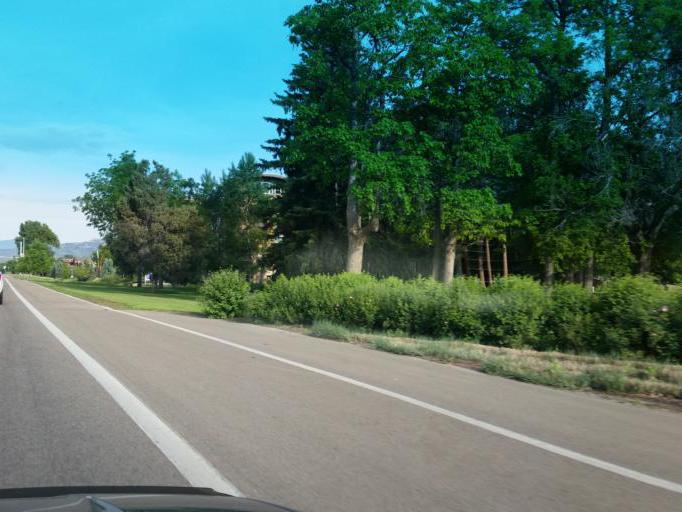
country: US
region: Colorado
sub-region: Larimer County
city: Fort Collins
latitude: 40.5234
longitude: -105.0286
